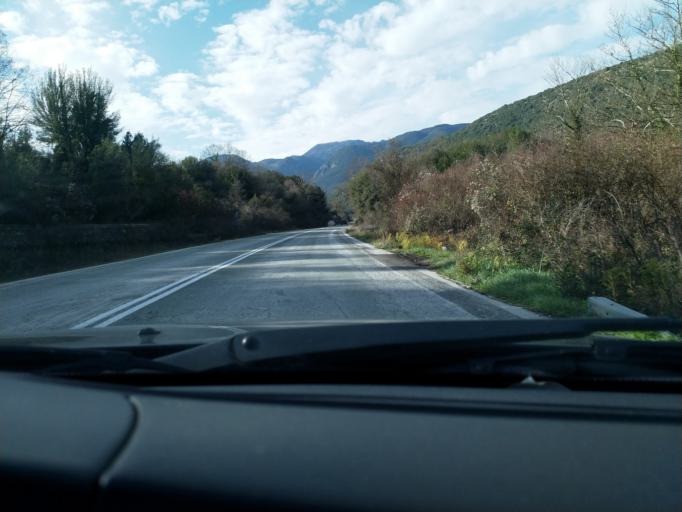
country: GR
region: Epirus
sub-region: Nomos Ioanninon
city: Agia Kyriaki
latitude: 39.4488
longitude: 20.8644
